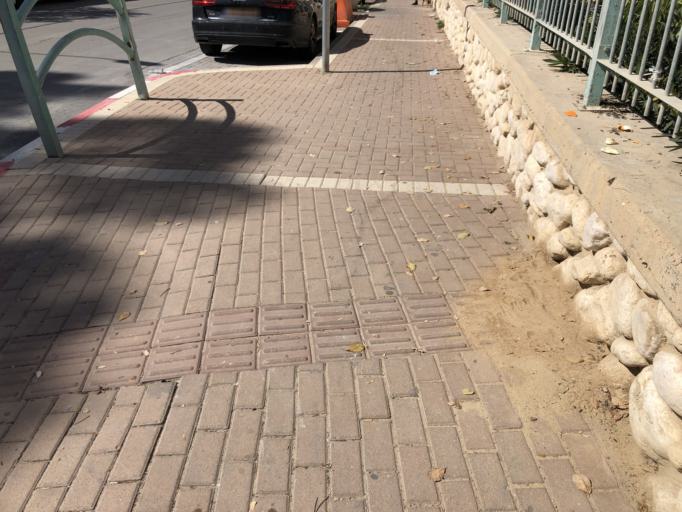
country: IL
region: Southern District
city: Dimona
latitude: 31.0653
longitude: 35.0393
